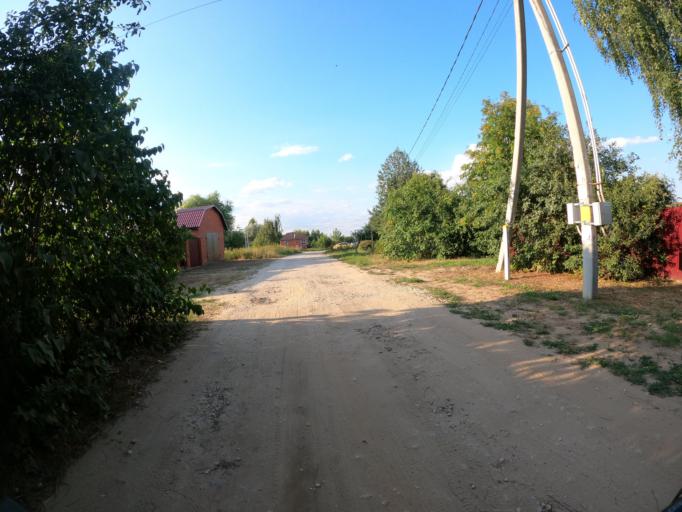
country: RU
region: Moskovskaya
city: Bronnitsy
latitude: 55.4844
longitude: 38.2594
